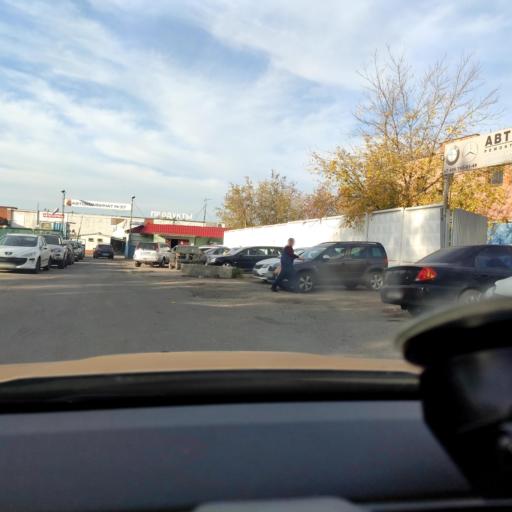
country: RU
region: Moscow
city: Mikhalkovo
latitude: 55.6938
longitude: 37.4236
